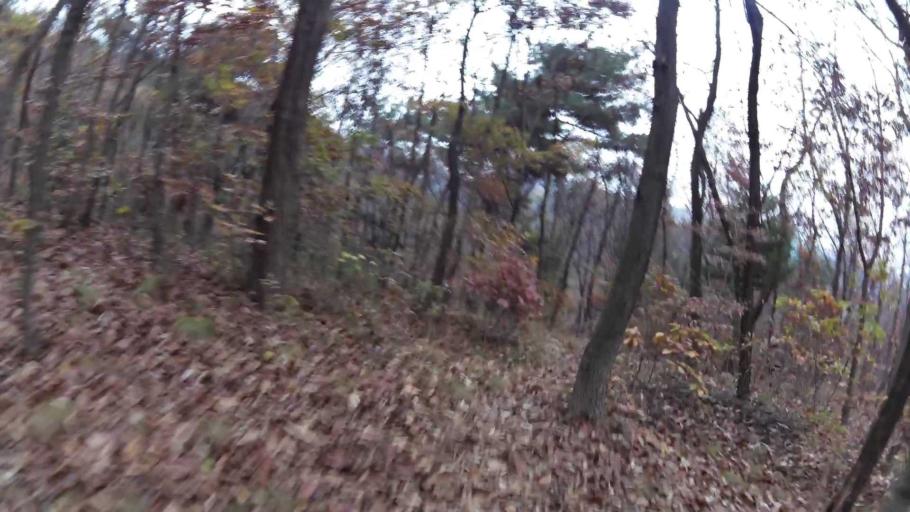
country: KR
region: Daegu
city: Daegu
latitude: 35.8587
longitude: 128.6580
